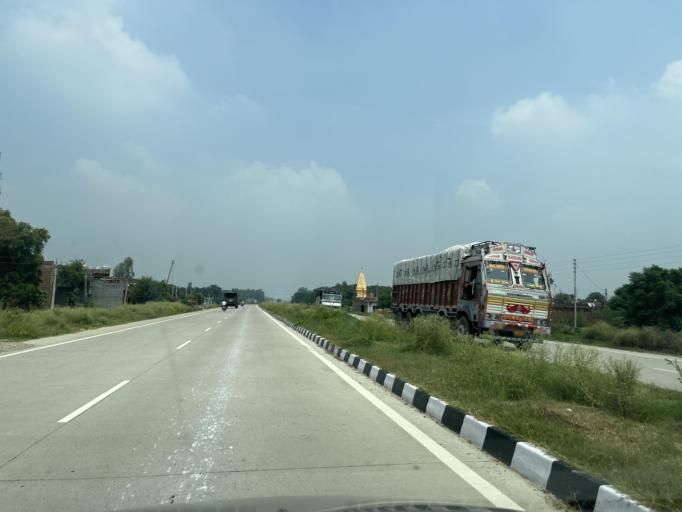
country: IN
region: Uttar Pradesh
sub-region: Bijnor
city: Najibabad
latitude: 29.5477
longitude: 78.3395
